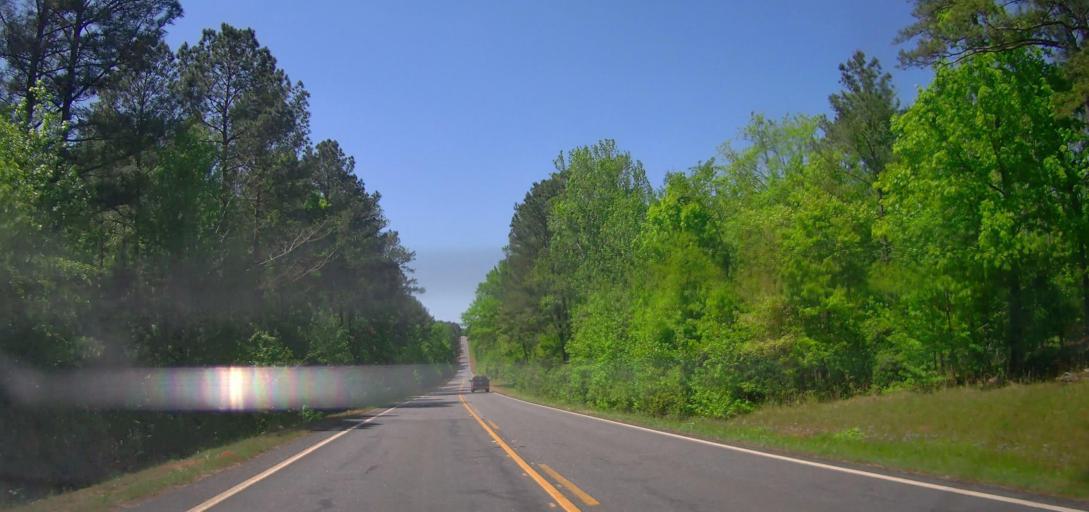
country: US
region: Georgia
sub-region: Putnam County
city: Eatonton
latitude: 33.2086
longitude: -83.4746
